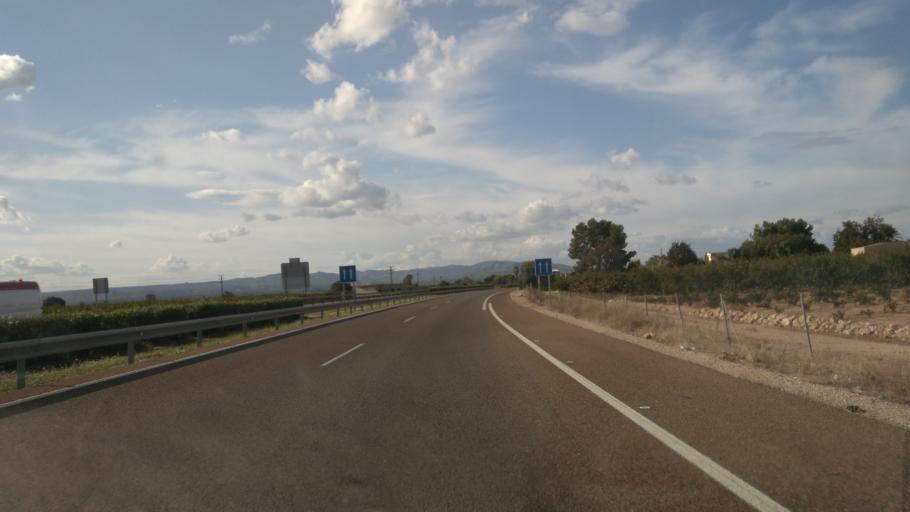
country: ES
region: Valencia
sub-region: Provincia de Valencia
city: Guadassuar
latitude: 39.1786
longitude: -0.4817
